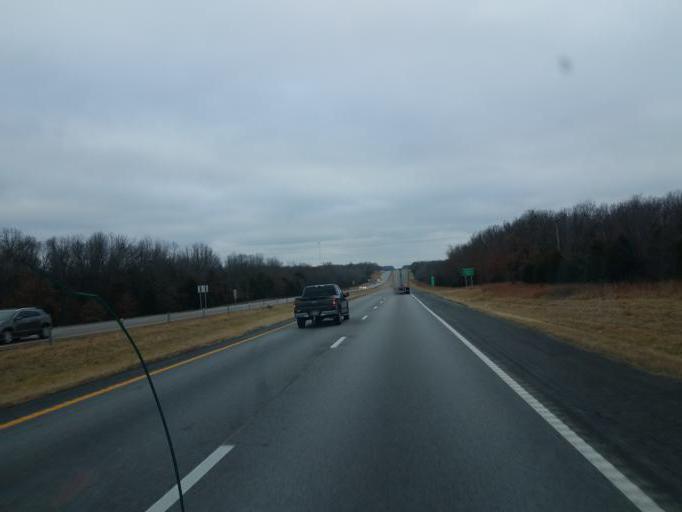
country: US
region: Missouri
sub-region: Webster County
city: Marshfield
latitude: 37.4849
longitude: -92.8517
